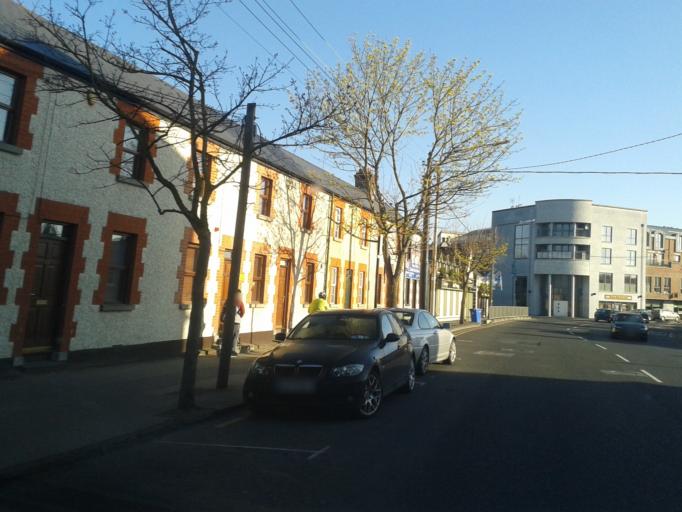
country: IE
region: Leinster
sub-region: Fingal County
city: Swords
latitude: 53.4625
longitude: -6.2182
